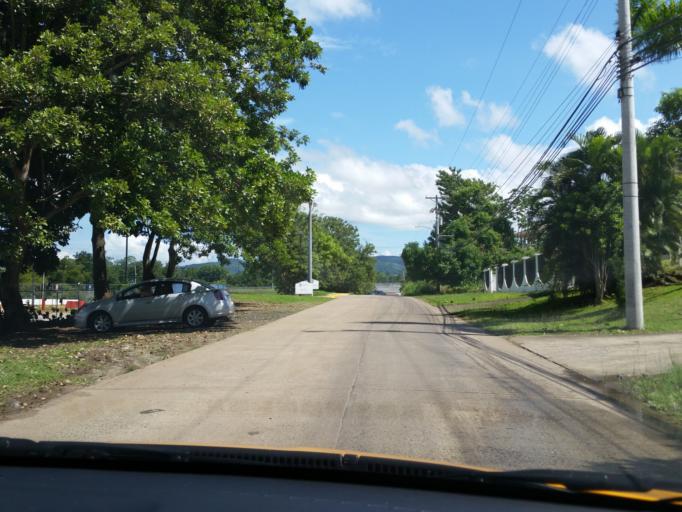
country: PA
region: Panama
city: San Miguelito
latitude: 9.0782
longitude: -79.4705
